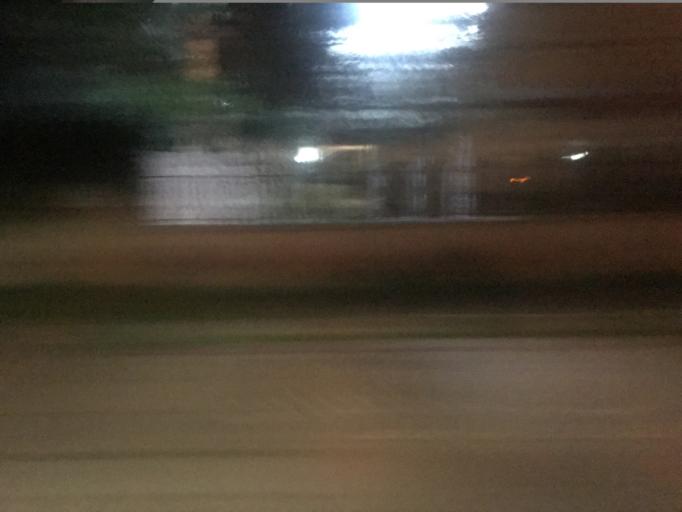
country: TR
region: Istanbul
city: Bahcelievler
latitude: 40.9810
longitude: 28.8677
